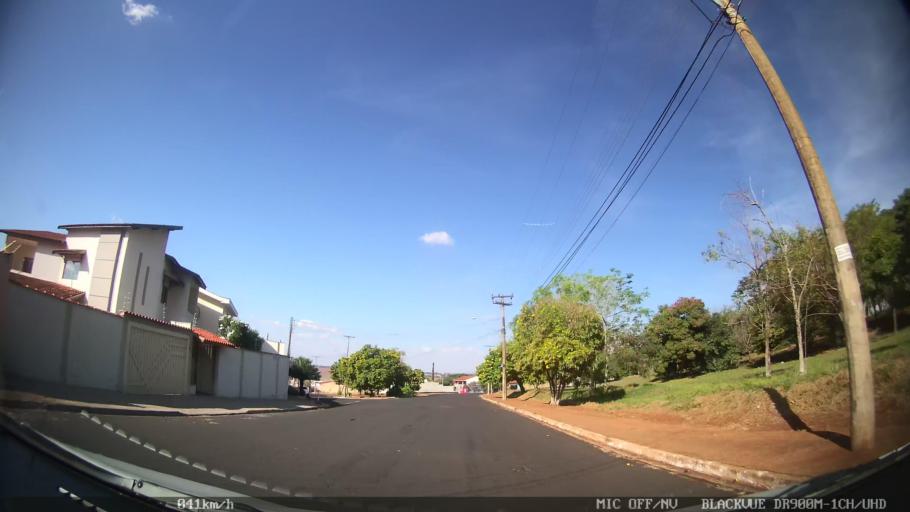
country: BR
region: Sao Paulo
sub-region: Ribeirao Preto
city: Ribeirao Preto
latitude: -21.1759
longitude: -47.7685
